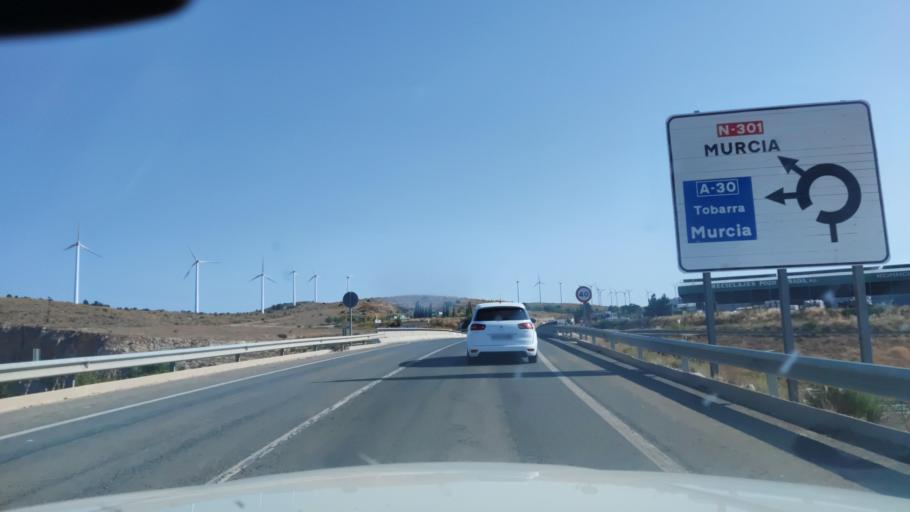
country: ES
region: Castille-La Mancha
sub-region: Provincia de Albacete
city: Pozo-Canada
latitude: 38.7938
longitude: -1.7257
